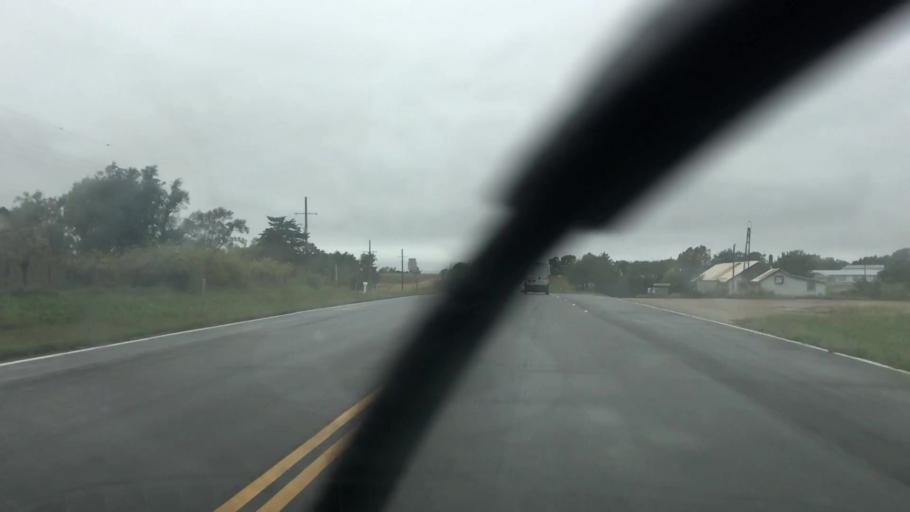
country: US
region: Kansas
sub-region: Anderson County
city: Garnett
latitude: 38.1697
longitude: -95.2866
